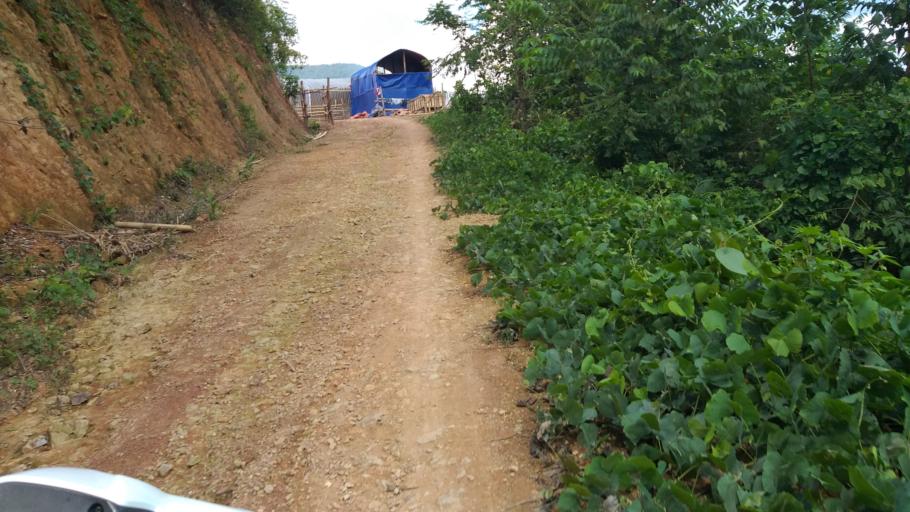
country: LA
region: Phongsali
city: Khoa
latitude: 21.2731
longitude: 102.5201
